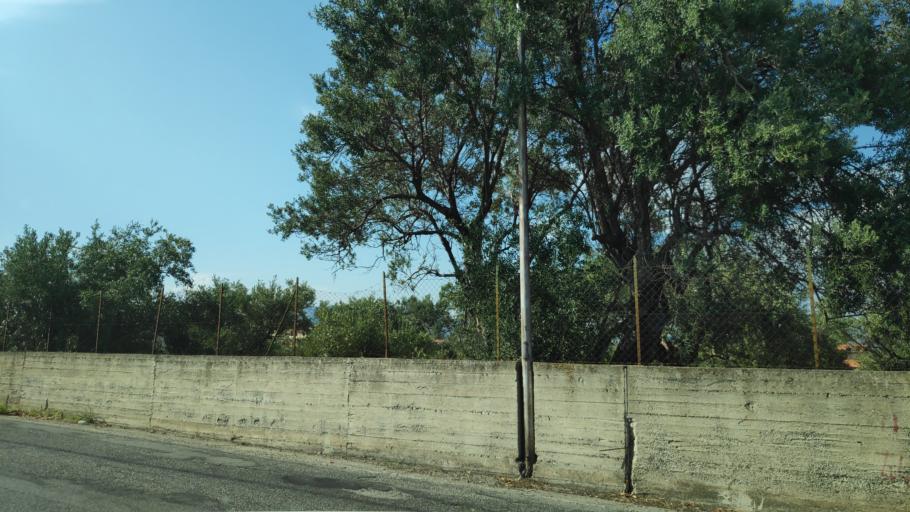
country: IT
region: Calabria
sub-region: Provincia di Catanzaro
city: Soverato Superiore
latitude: 38.6875
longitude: 16.5367
